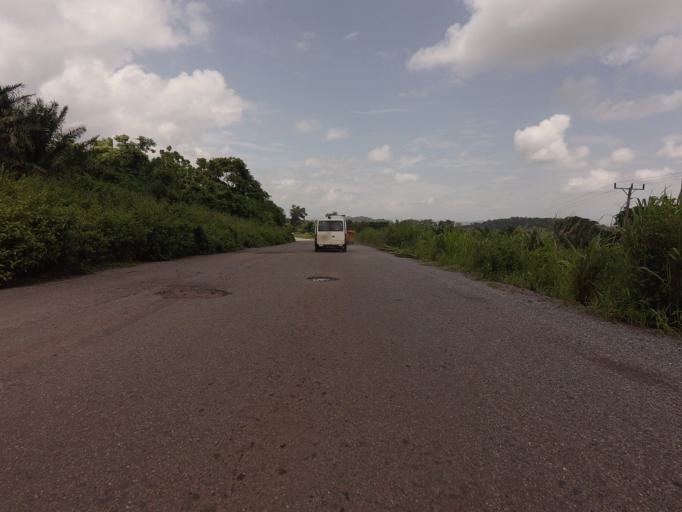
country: GH
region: Volta
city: Ho
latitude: 6.7870
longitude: 0.3671
